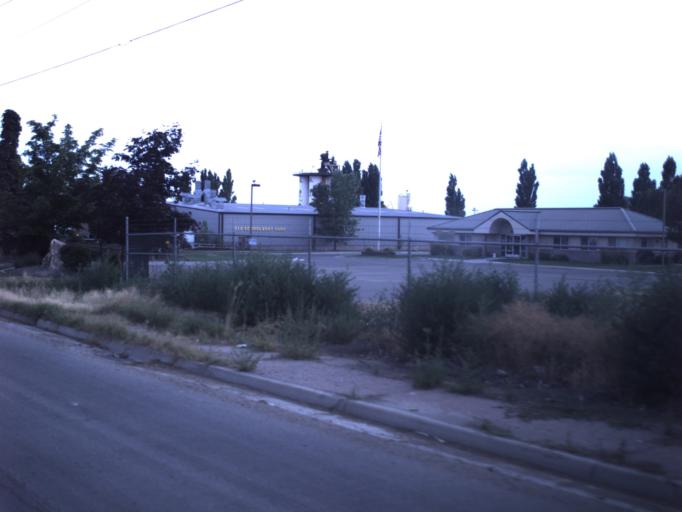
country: US
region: Utah
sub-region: Weber County
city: Marriott-Slaterville
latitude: 41.2401
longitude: -112.0255
